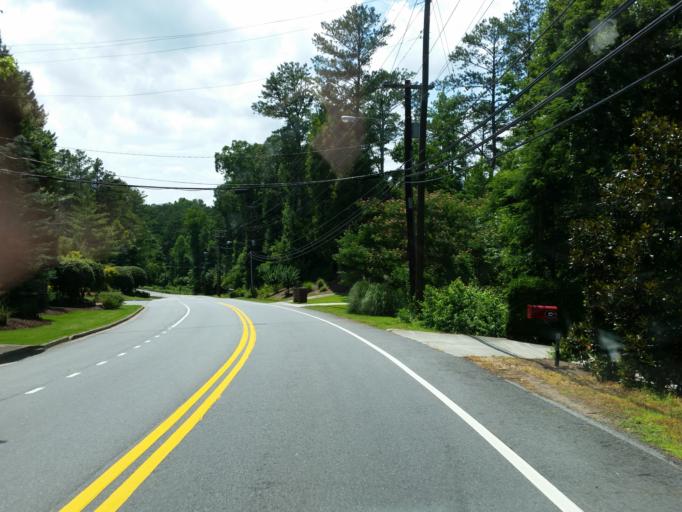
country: US
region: Georgia
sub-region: Fulton County
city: Roswell
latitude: 34.0294
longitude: -84.3934
